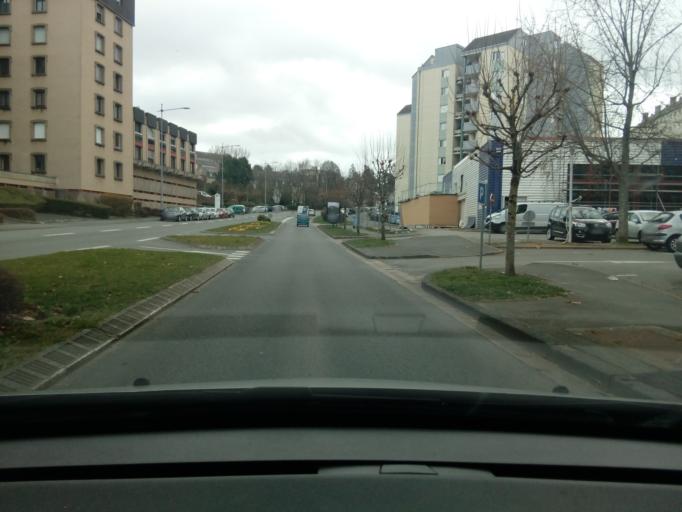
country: FR
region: Limousin
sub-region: Departement de la Creuse
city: Gueret
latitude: 46.1714
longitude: 1.8741
